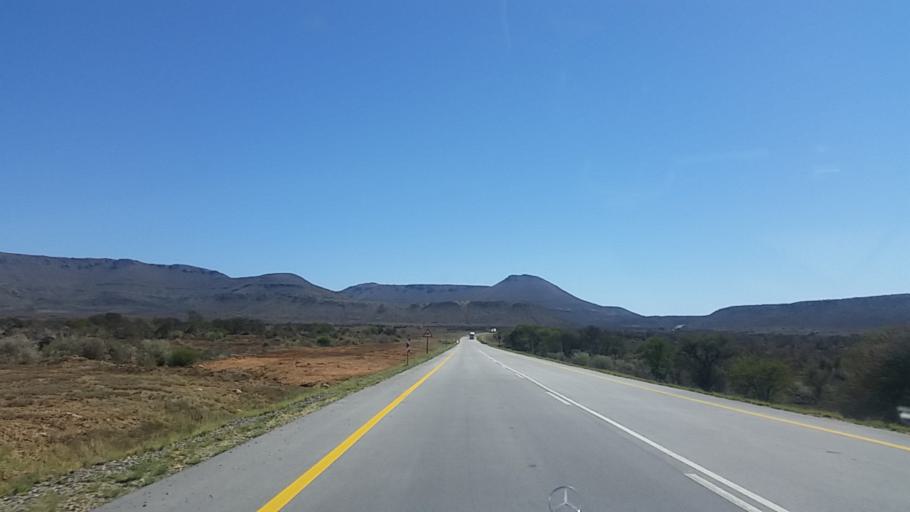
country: ZA
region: Eastern Cape
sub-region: Cacadu District Municipality
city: Graaff-Reinet
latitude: -32.0888
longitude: 24.6031
